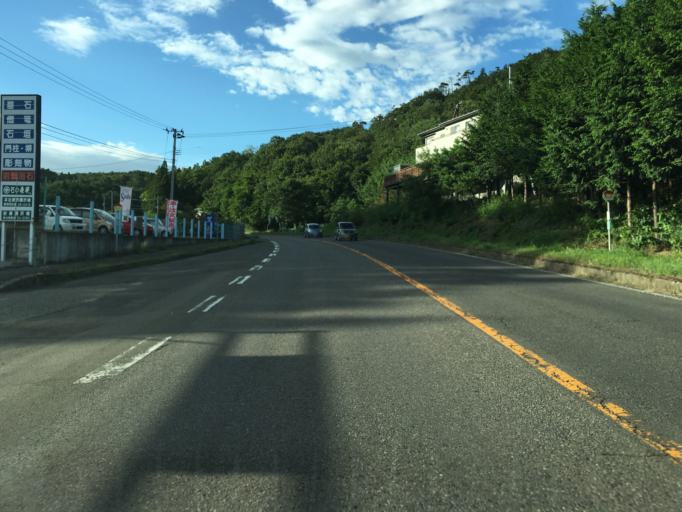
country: JP
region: Fukushima
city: Nihommatsu
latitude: 37.6372
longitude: 140.4647
